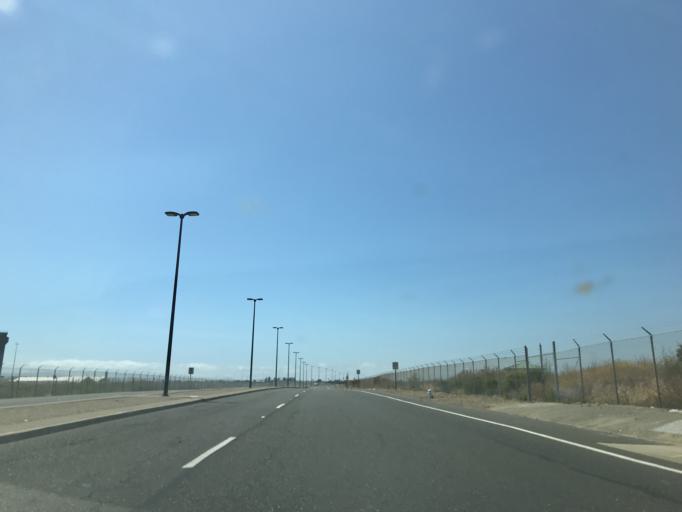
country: US
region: California
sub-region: Alameda County
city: Alameda
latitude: 37.7216
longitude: -122.2110
